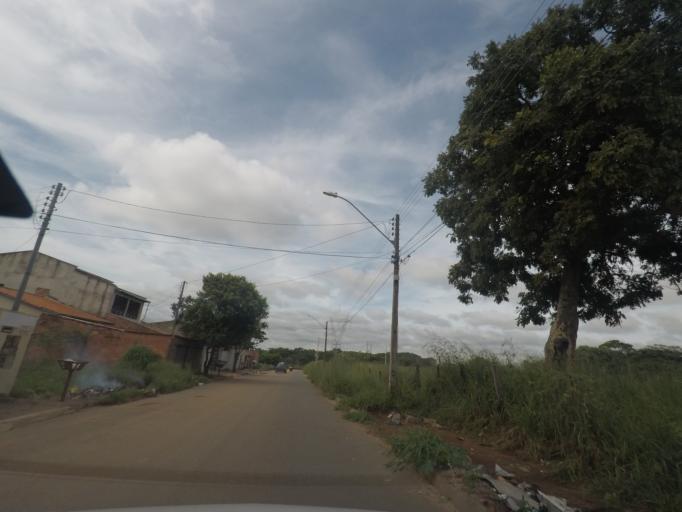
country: BR
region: Goias
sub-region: Goiania
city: Goiania
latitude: -16.6713
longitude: -49.1846
